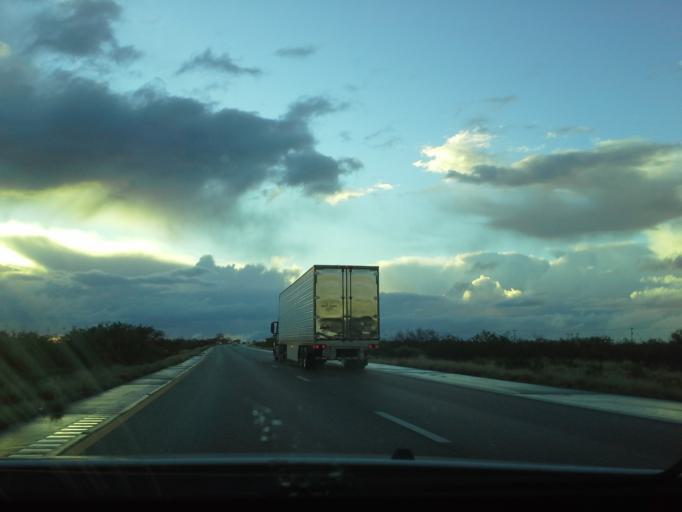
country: US
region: Arizona
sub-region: Pima County
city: Vail
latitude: 32.0449
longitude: -110.7450
